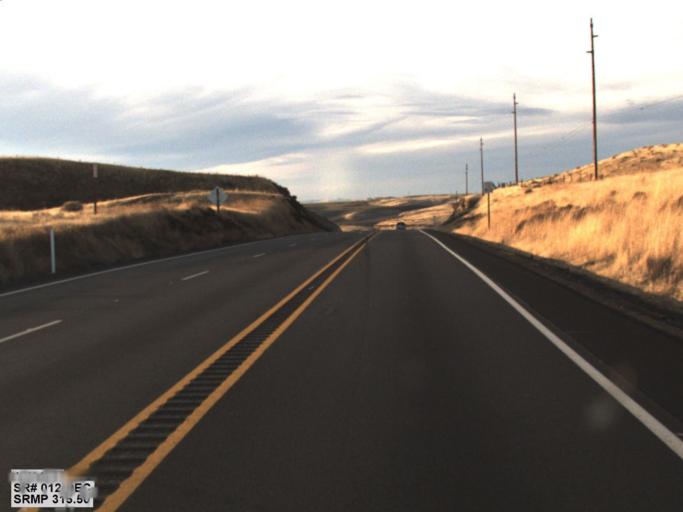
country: US
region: Washington
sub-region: Walla Walla County
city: Burbank
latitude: 46.0660
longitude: -118.7556
